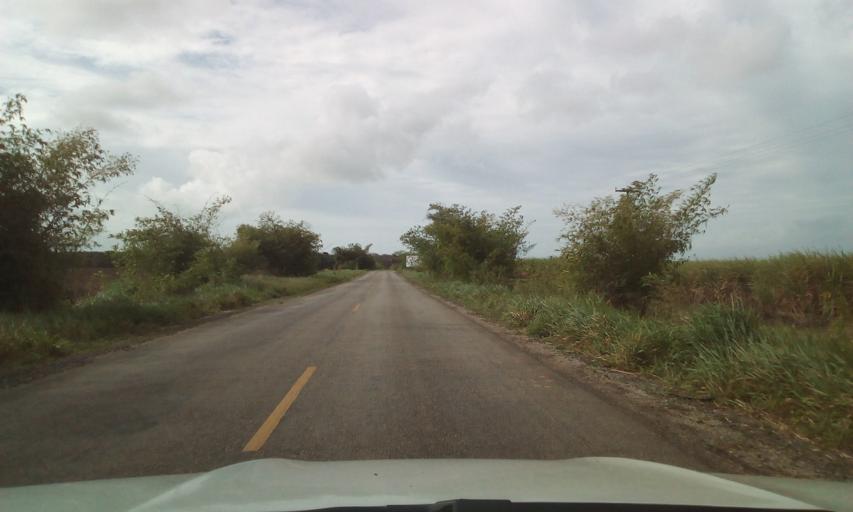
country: BR
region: Paraiba
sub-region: Cabedelo
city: Cabedelo
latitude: -6.9302
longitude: -34.9017
